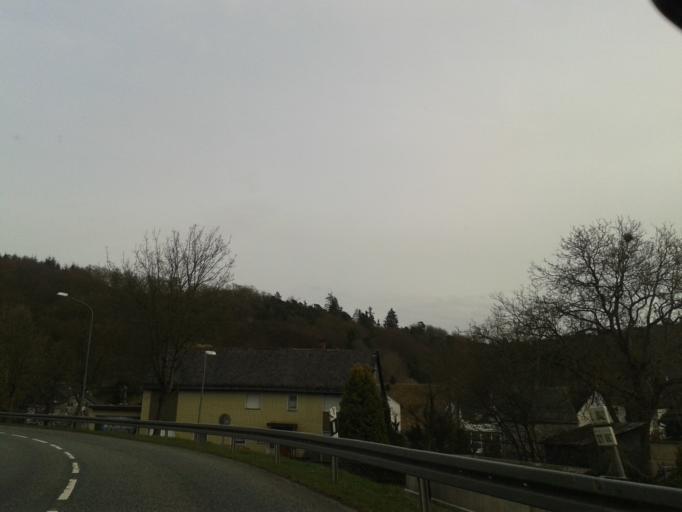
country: DE
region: Hesse
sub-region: Regierungsbezirk Giessen
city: Siegbach
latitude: 50.8091
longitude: 8.4377
